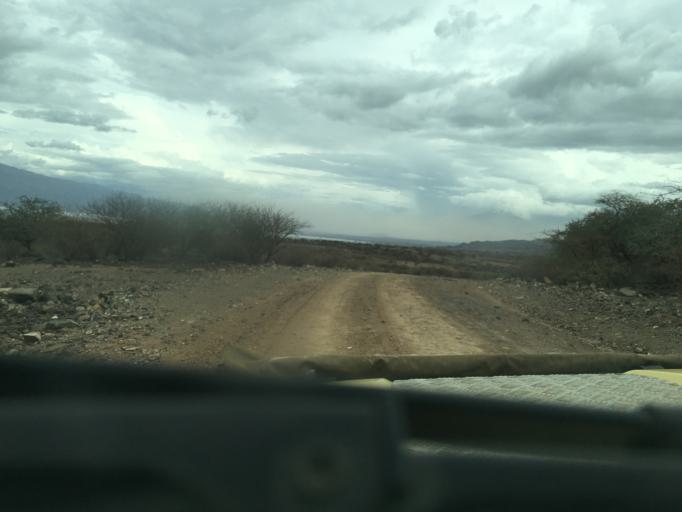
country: KE
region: Kajiado
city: Magadi
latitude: -2.4783
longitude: 35.8748
